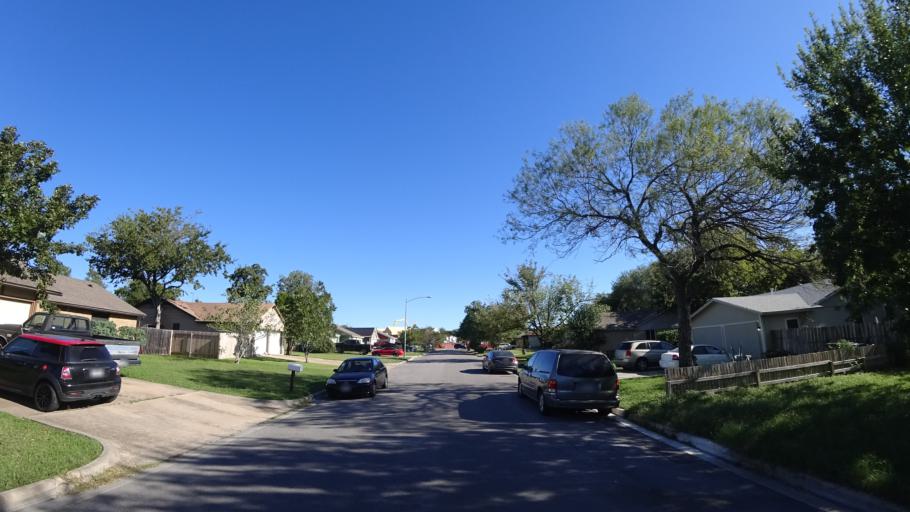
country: US
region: Texas
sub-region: Travis County
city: Austin
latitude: 30.3146
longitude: -97.6584
